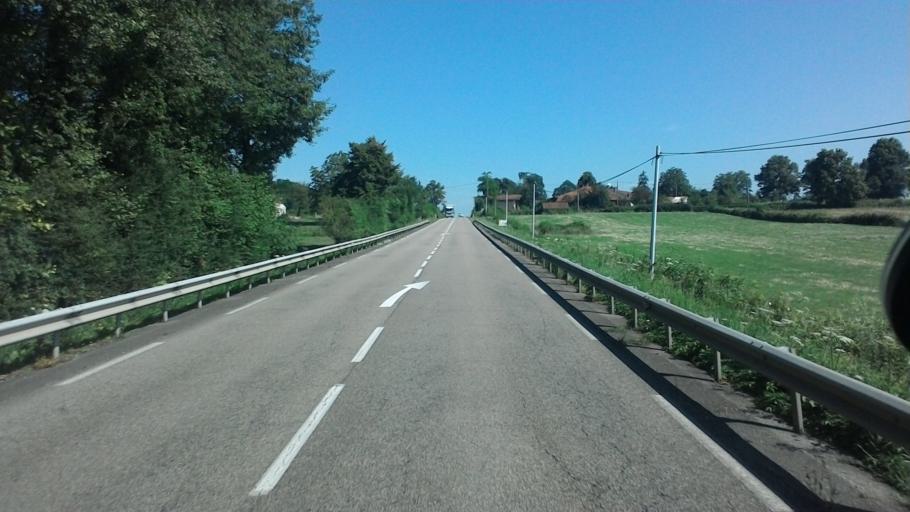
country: FR
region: Bourgogne
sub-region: Departement de Saone-et-Loire
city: Romenay
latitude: 46.4841
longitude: 5.0719
